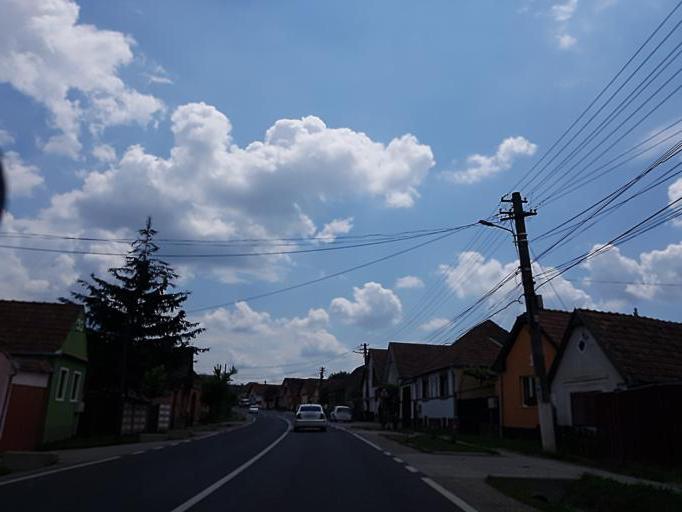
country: RO
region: Sibiu
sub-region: Comuna Slimnic
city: Slimnic
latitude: 45.9123
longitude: 24.1542
